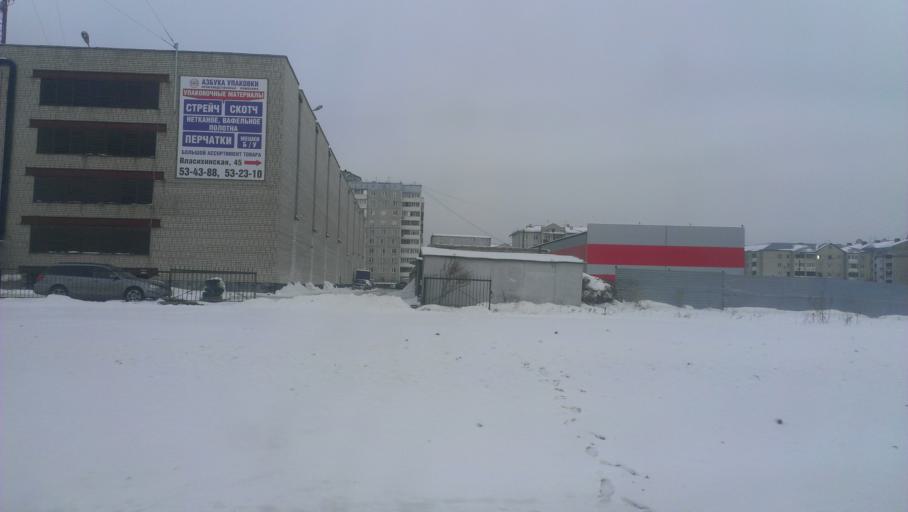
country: RU
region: Altai Krai
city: Novosilikatnyy
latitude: 53.3296
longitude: 83.6699
